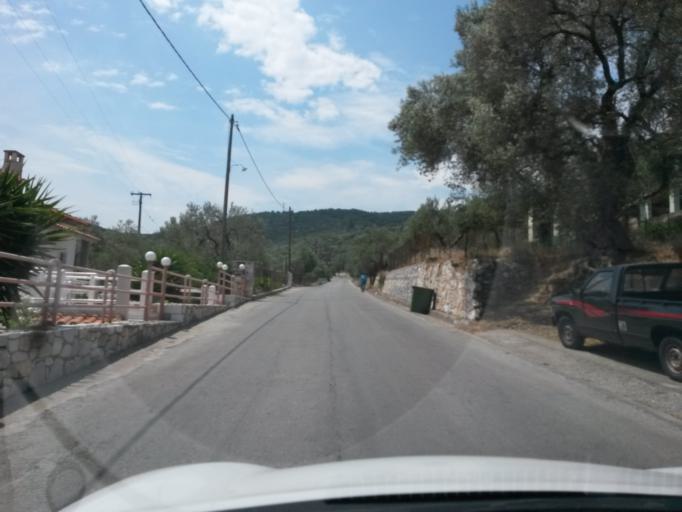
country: GR
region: North Aegean
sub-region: Nomos Lesvou
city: Pamfylla
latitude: 39.1814
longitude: 26.4830
